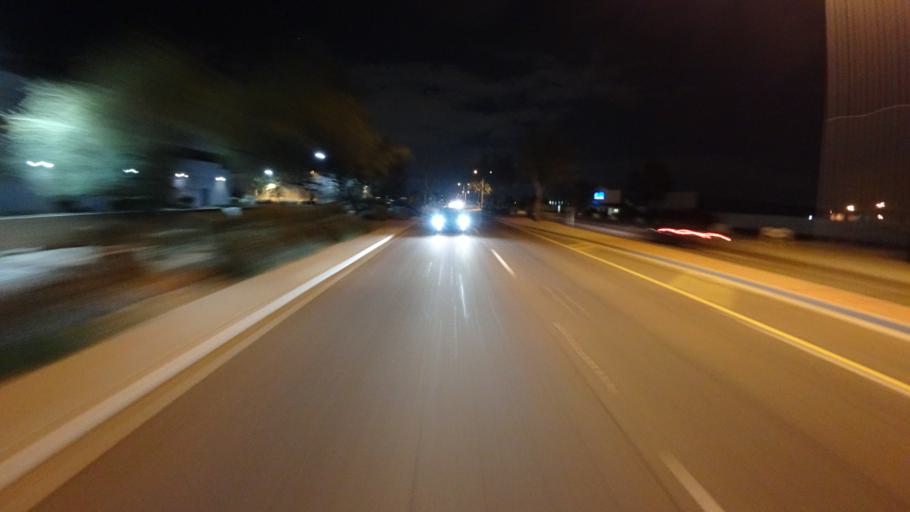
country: US
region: Arizona
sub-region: Maricopa County
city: Guadalupe
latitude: 33.3072
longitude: -111.9632
